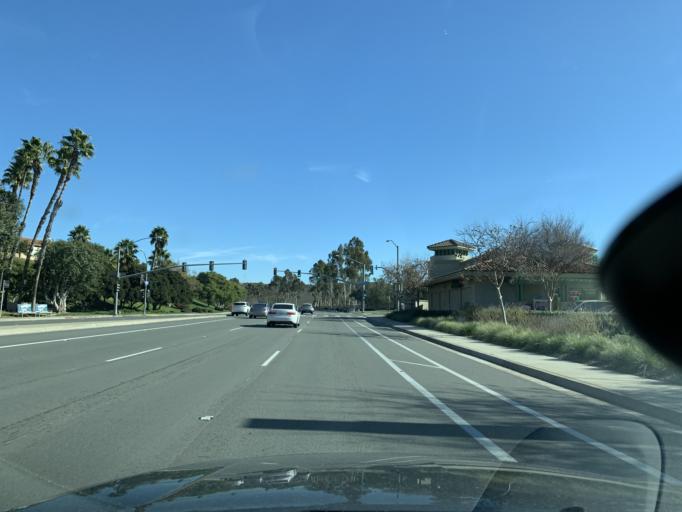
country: US
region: California
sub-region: San Diego County
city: Poway
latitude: 32.9458
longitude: -117.0850
